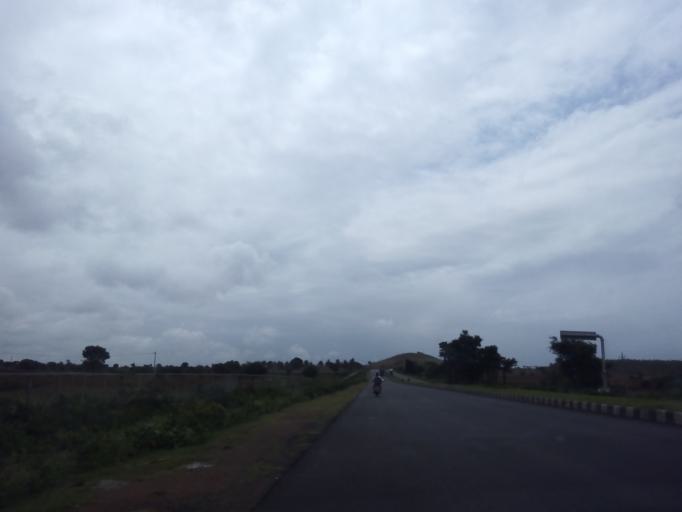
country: IN
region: Karnataka
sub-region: Haveri
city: Byadgi
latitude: 14.7164
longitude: 75.4930
